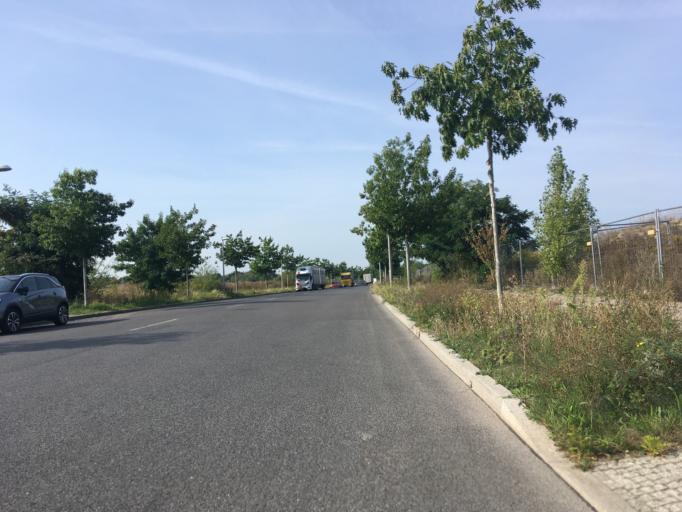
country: DE
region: Berlin
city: Altglienicke
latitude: 52.3937
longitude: 13.5395
